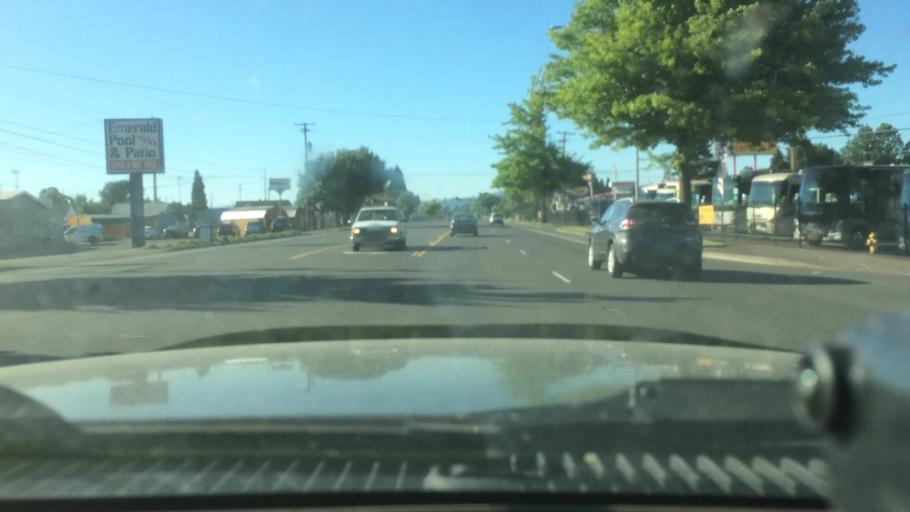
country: US
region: Oregon
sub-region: Lane County
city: Eugene
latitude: 44.0827
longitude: -123.1534
